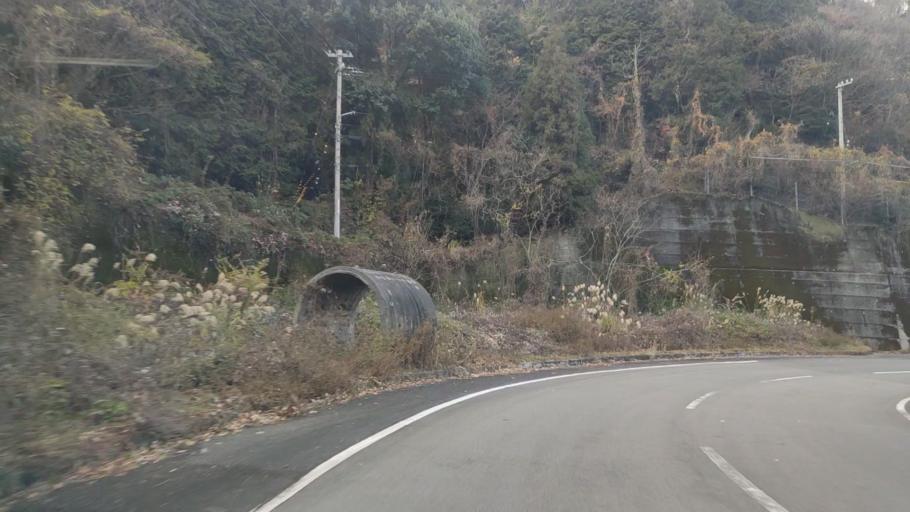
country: JP
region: Ehime
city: Saijo
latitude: 33.8812
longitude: 133.1325
